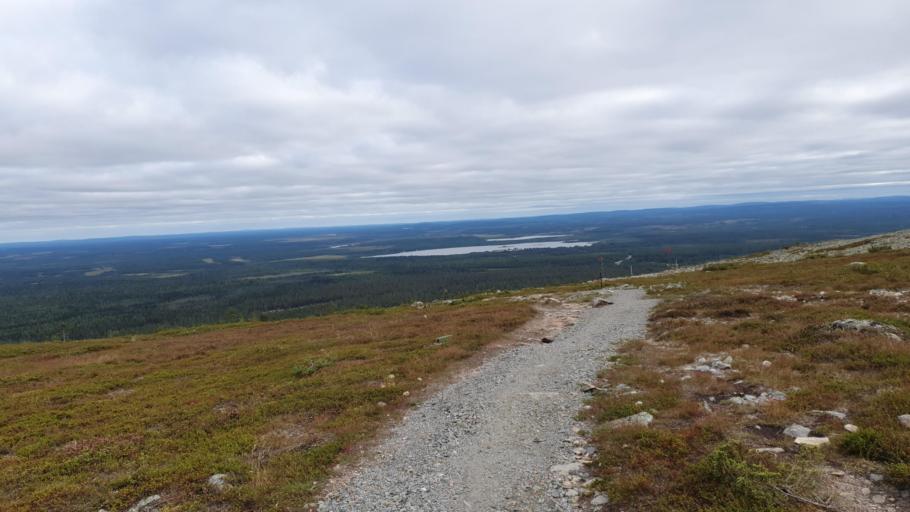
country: FI
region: Lapland
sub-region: Tunturi-Lappi
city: Kolari
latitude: 67.5662
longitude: 24.2496
